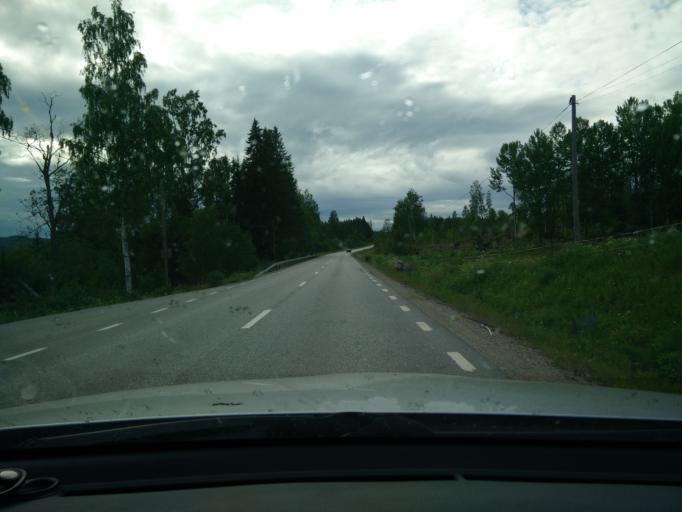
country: SE
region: Gaevleborg
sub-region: Nordanstigs Kommun
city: Bergsjoe
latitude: 62.0877
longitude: 16.7851
